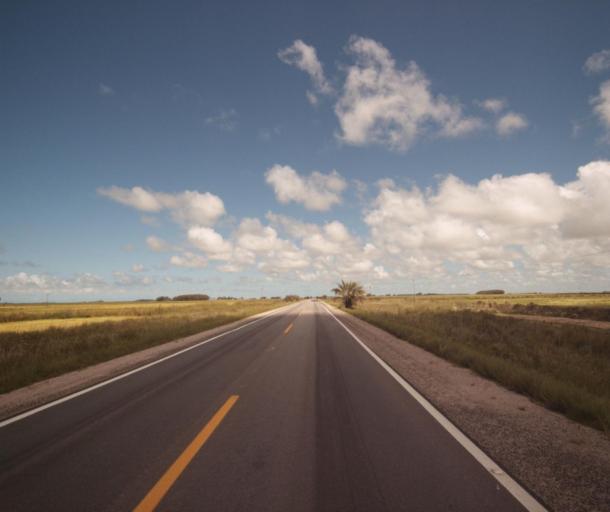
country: UY
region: Cerro Largo
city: Rio Branco
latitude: -32.8960
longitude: -52.7271
